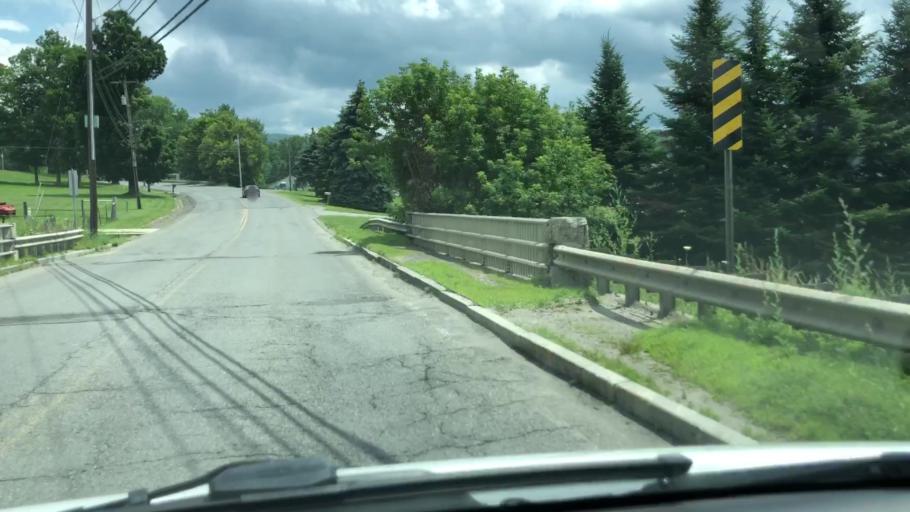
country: US
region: Massachusetts
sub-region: Berkshire County
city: Adams
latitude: 42.5892
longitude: -73.1132
